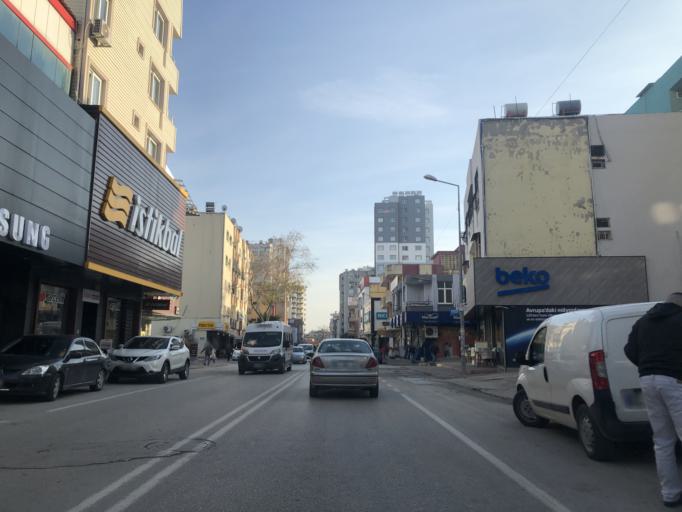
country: TR
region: Adana
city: Adana
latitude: 37.0242
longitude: 35.3127
